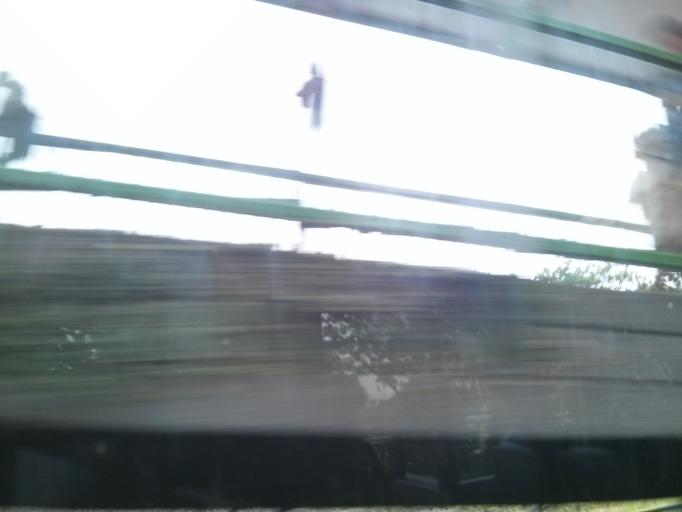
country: SG
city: Singapore
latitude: 1.2963
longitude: 103.7846
